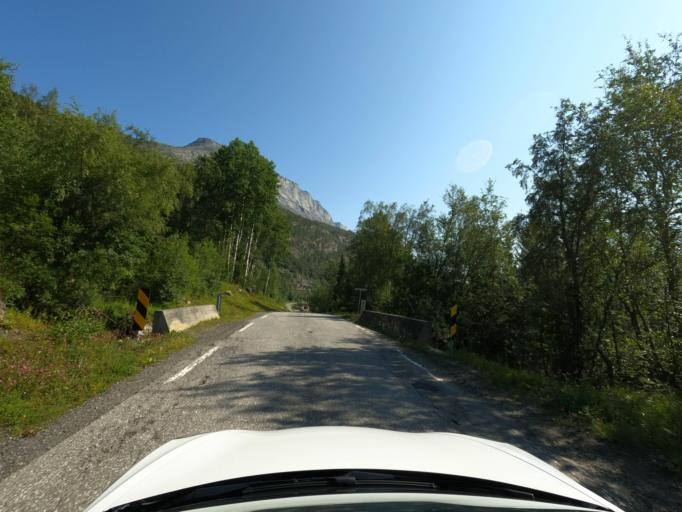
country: NO
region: Nordland
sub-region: Narvik
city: Narvik
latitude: 68.2761
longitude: 17.3907
